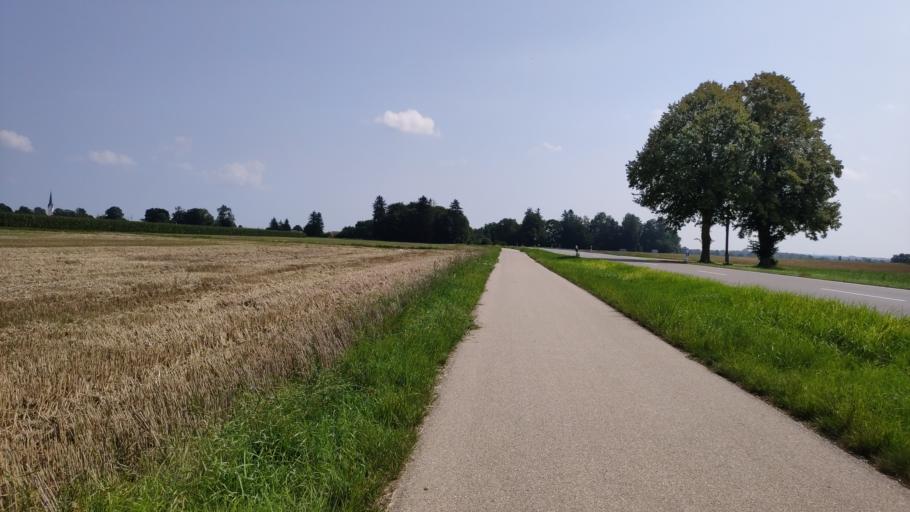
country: DE
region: Bavaria
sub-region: Swabia
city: Kleinaitingen
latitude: 48.2166
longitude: 10.8309
